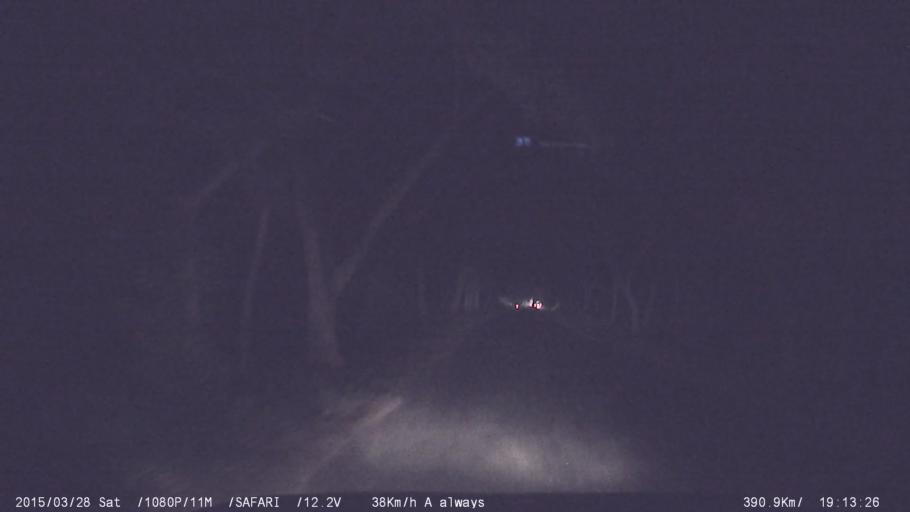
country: IN
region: Karnataka
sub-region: Mandya
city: Shrirangapattana
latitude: 12.3986
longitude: 76.6369
